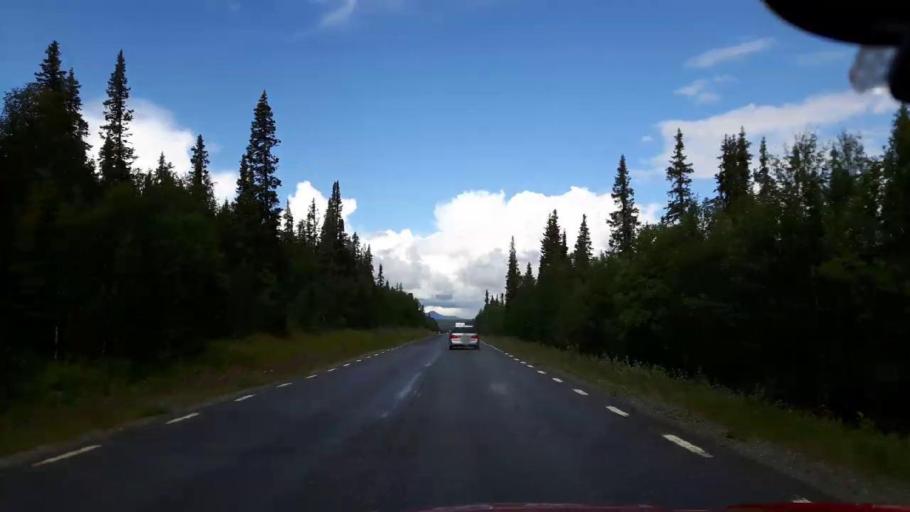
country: SE
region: Vaesterbotten
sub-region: Vilhelmina Kommun
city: Sjoberg
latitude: 65.0268
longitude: 15.1478
